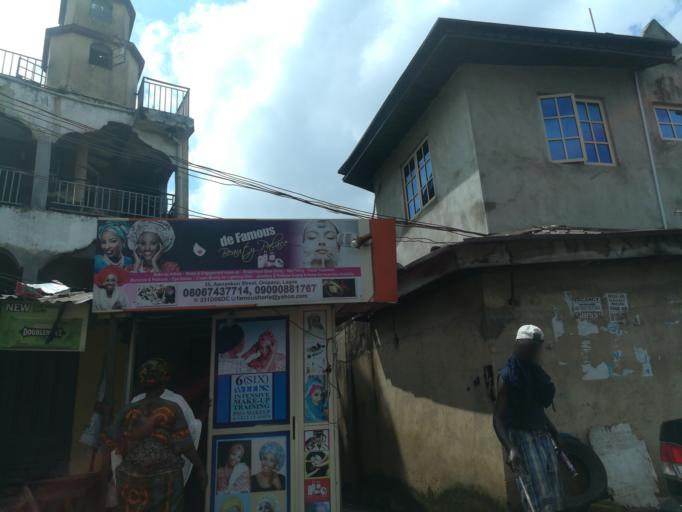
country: NG
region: Lagos
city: Somolu
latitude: 6.5358
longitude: 3.3633
